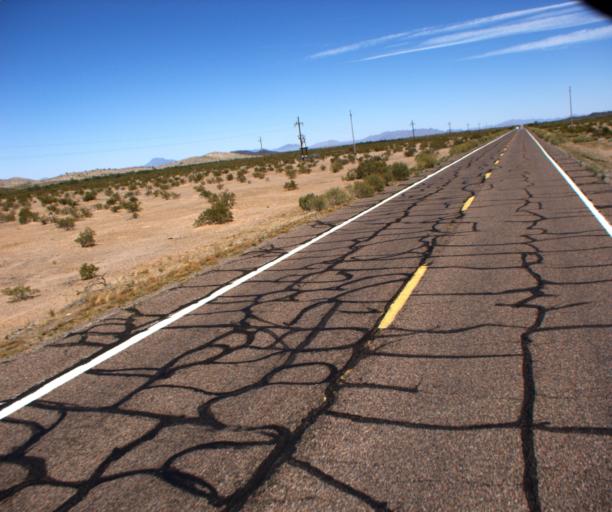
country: US
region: Arizona
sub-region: Maricopa County
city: Gila Bend
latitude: 32.7679
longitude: -112.8174
